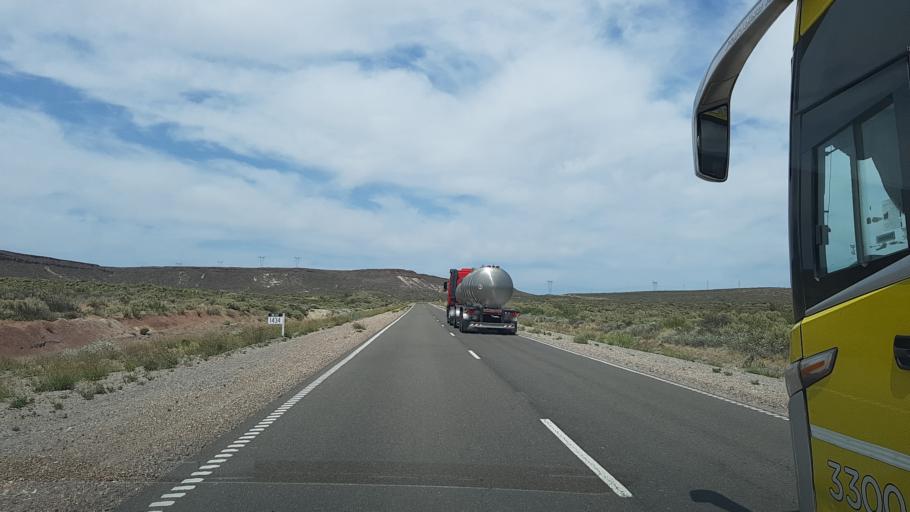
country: AR
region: Neuquen
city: Piedra del Aguila
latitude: -39.9693
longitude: -70.0158
